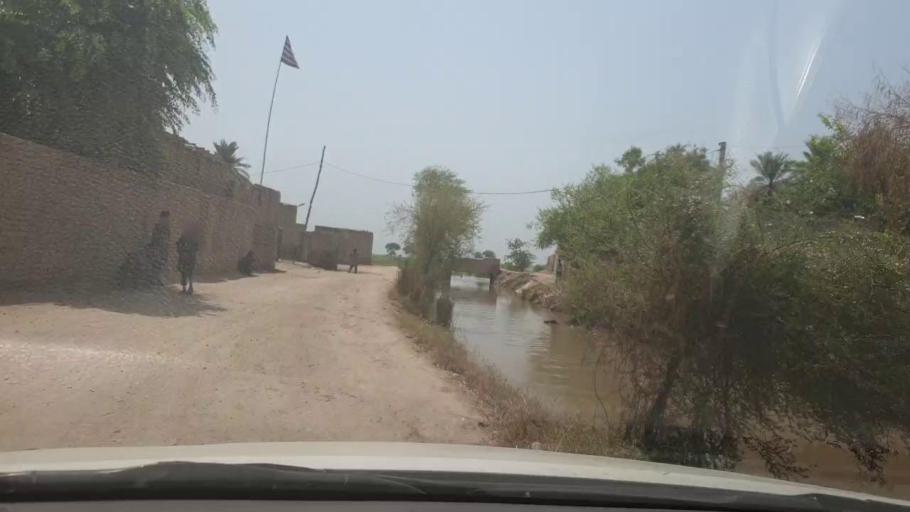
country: PK
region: Sindh
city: Shikarpur
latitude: 28.0518
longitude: 68.6047
